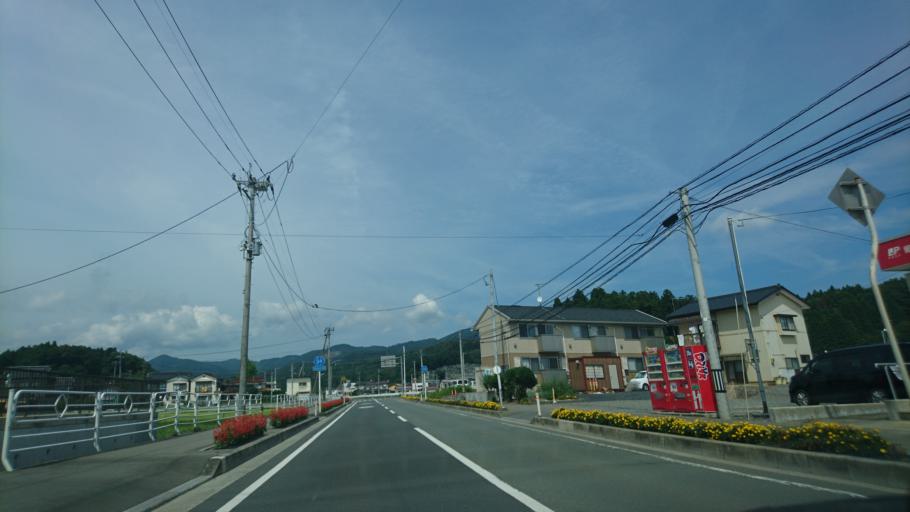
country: JP
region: Iwate
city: Ofunato
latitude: 38.9224
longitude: 141.5829
